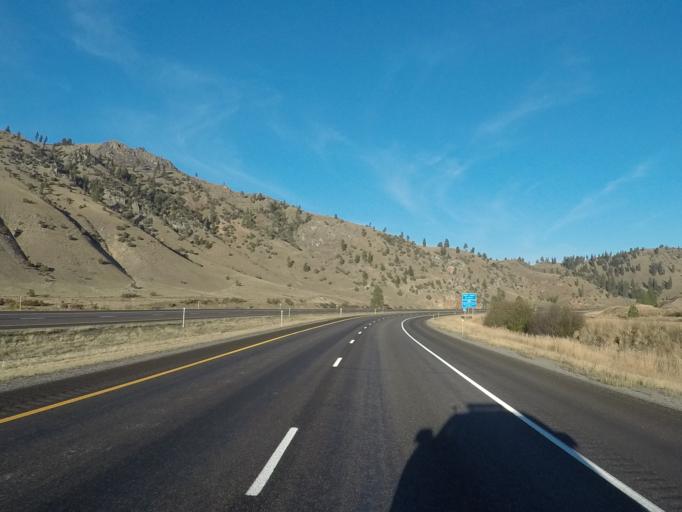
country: US
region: Montana
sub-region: Missoula County
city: Clinton
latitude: 46.7029
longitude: -113.3828
